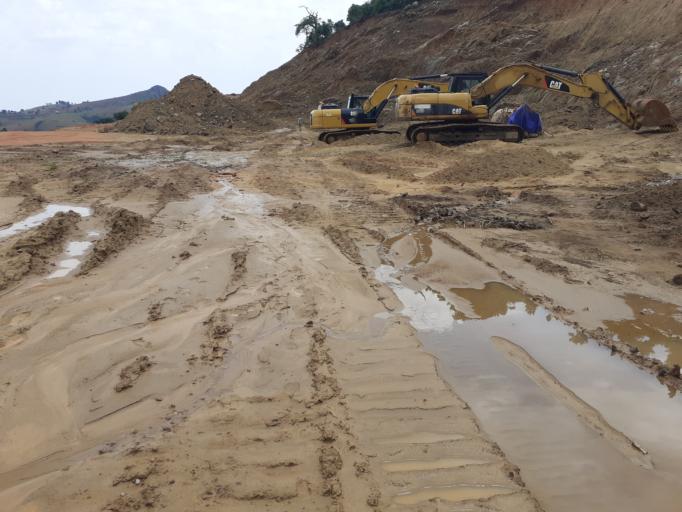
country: ET
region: Oromiya
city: Gimbi
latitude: 9.3278
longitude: 35.6925
